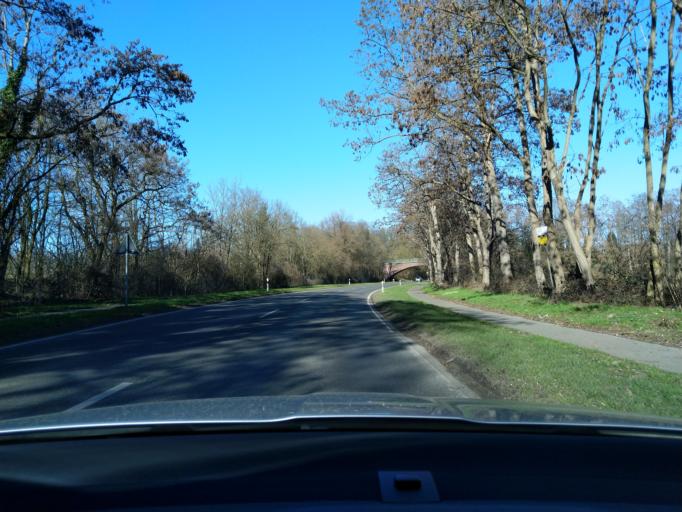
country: DE
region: North Rhine-Westphalia
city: Wegberg
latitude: 51.1418
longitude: 6.2677
